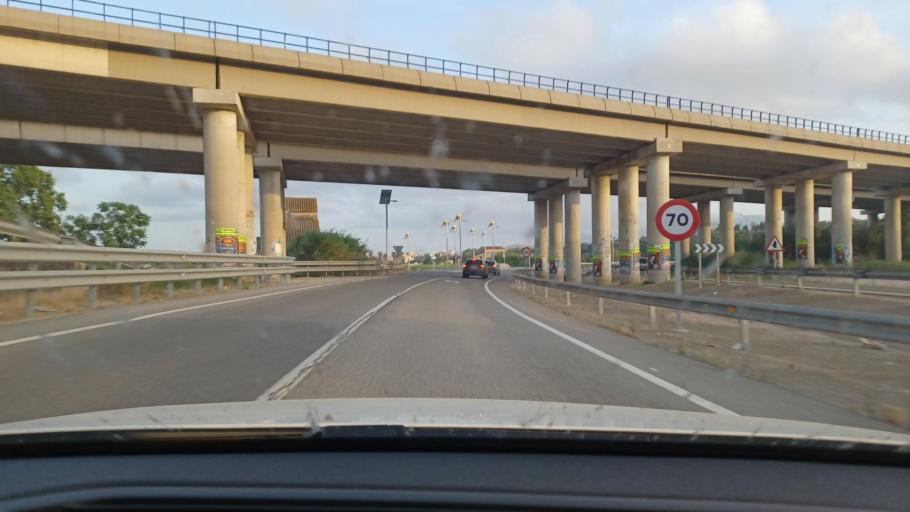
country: ES
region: Catalonia
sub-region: Provincia de Tarragona
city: Amposta
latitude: 40.7276
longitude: 0.5712
